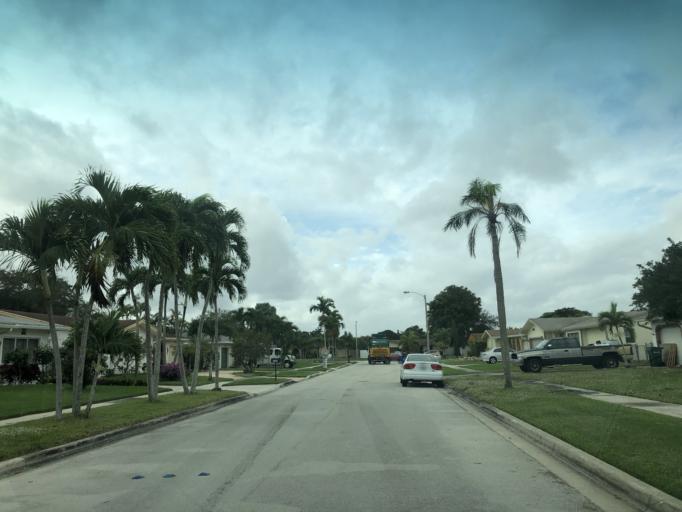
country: US
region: Florida
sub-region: Broward County
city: North Lauderdale
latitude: 26.2409
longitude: -80.2321
